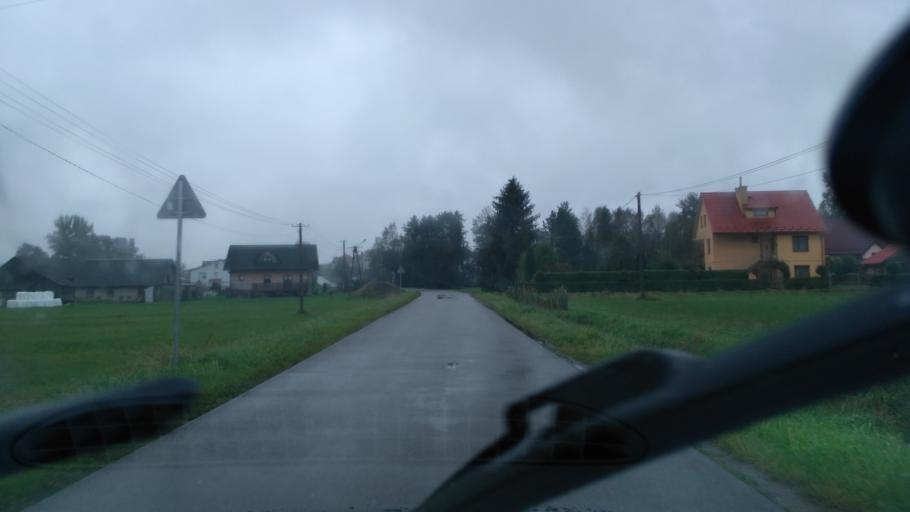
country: PL
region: Subcarpathian Voivodeship
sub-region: Powiat ropczycko-sedziszowski
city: Niedzwiada
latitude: 50.0028
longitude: 21.5501
